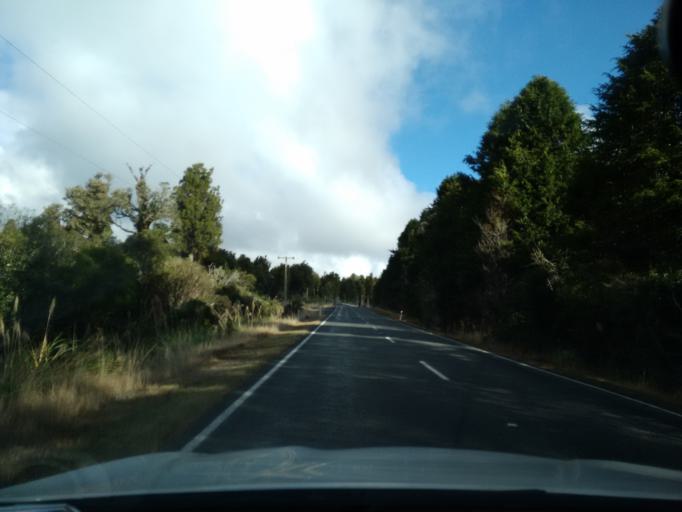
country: NZ
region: Manawatu-Wanganui
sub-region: Ruapehu District
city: Waiouru
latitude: -39.2404
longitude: 175.3917
